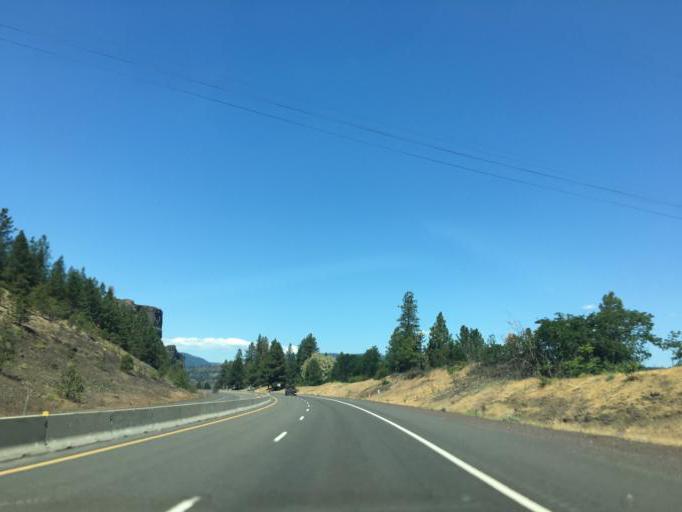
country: US
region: Oregon
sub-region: Wasco County
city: Chenoweth
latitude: 45.6819
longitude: -121.2907
